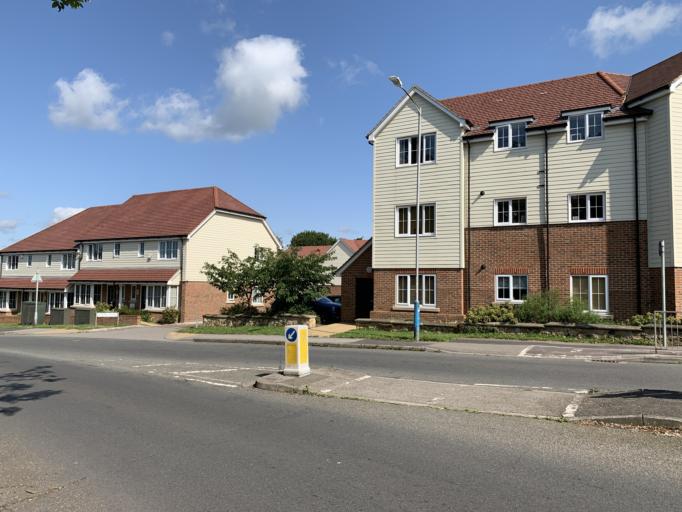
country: GB
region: England
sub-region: Kent
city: Tonbridge
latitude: 51.2099
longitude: 0.2787
